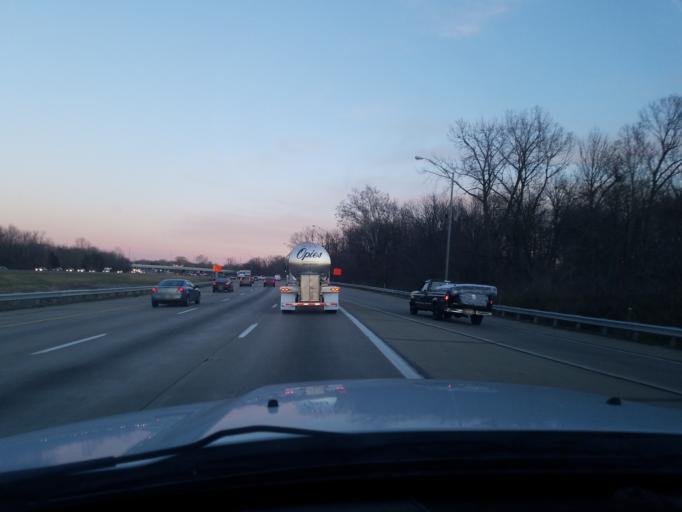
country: US
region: Indiana
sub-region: Marion County
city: Southport
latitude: 39.6979
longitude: -86.1449
